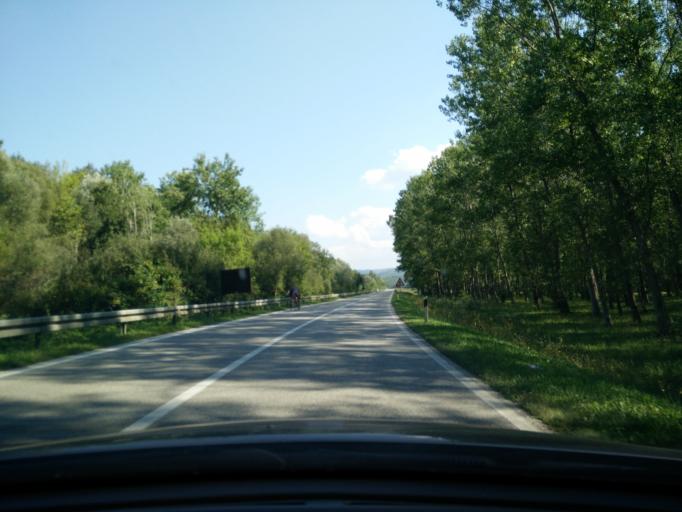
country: HR
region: Istarska
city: Karojba
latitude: 45.3515
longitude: 13.7707
